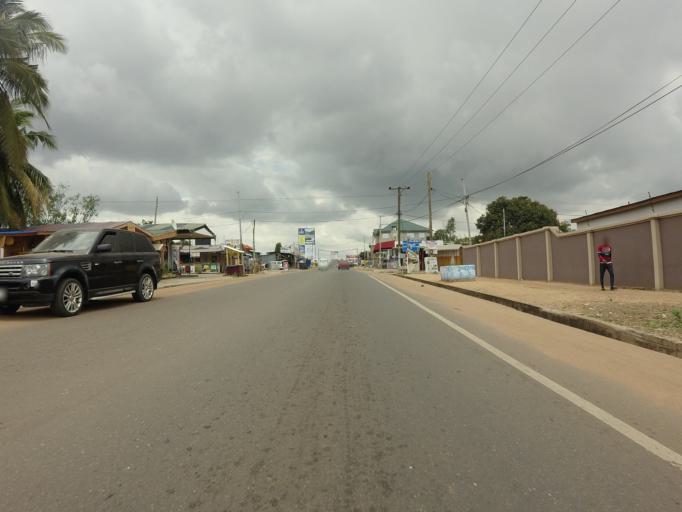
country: GH
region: Greater Accra
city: Medina Estates
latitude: 5.6848
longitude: -0.1501
